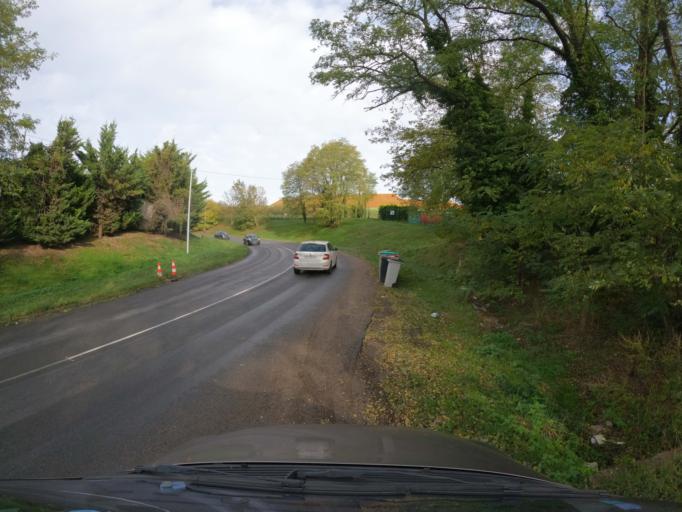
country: FR
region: Ile-de-France
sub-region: Departement de Seine-et-Marne
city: Courtry
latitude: 48.9242
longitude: 2.6075
